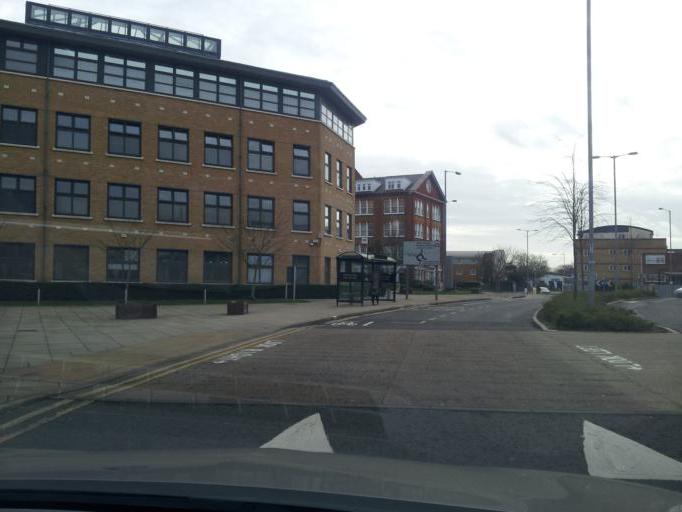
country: GB
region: England
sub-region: Essex
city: Chelmsford
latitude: 51.7414
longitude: 0.4736
